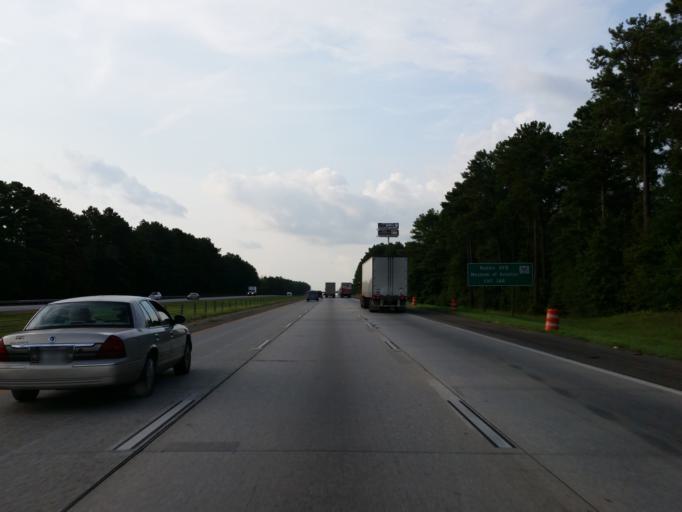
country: US
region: Georgia
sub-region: Houston County
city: Centerville
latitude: 32.5674
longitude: -83.7438
